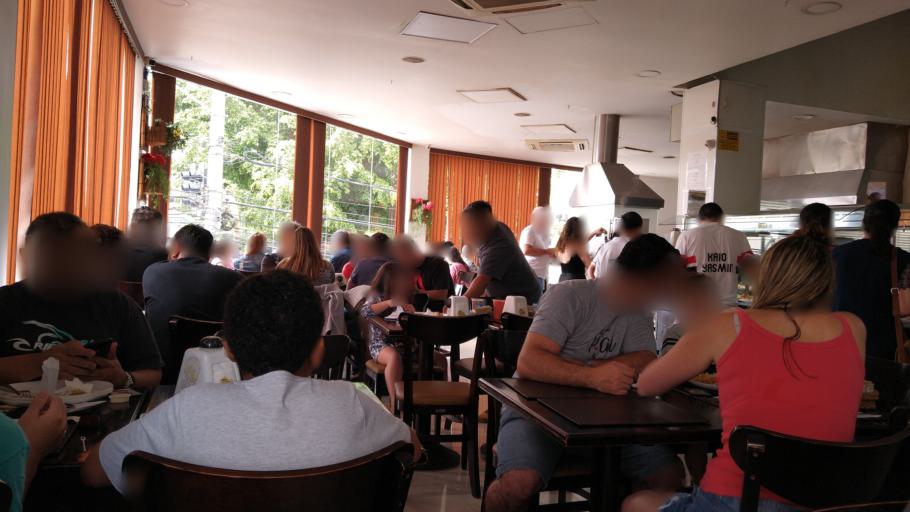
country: BR
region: Sao Paulo
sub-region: Sao Paulo
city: Sao Paulo
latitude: -23.4873
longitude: -46.6074
